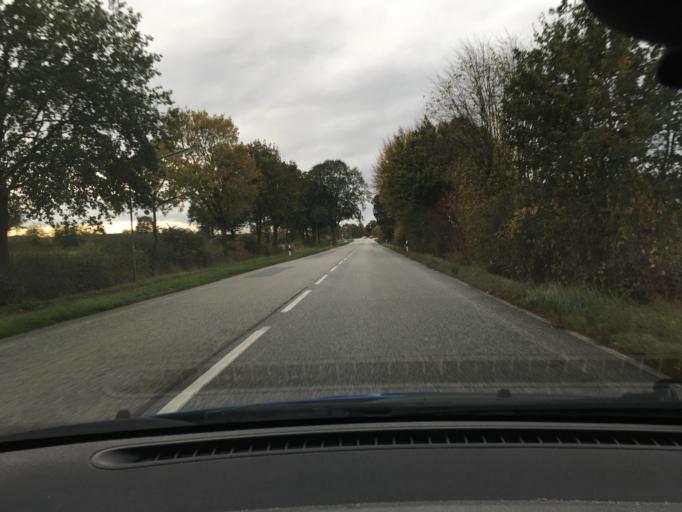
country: DE
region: Schleswig-Holstein
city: Hohenhorn
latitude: 53.4888
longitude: 10.3692
